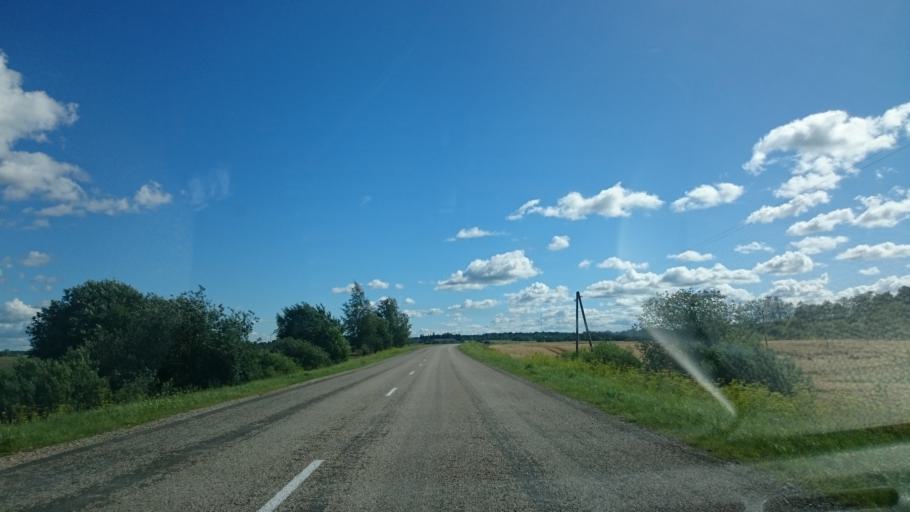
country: LV
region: Aizpute
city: Aizpute
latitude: 56.7568
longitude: 21.6157
